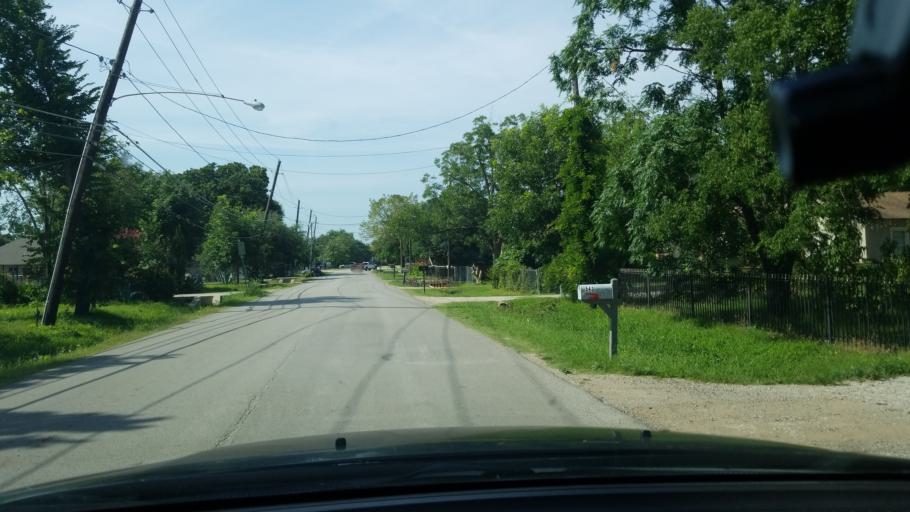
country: US
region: Texas
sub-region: Dallas County
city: Balch Springs
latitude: 32.7212
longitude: -96.6393
